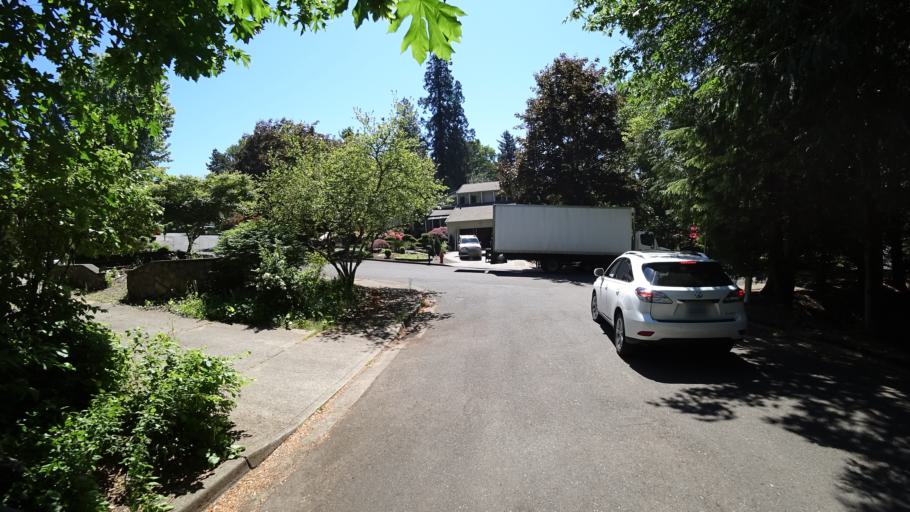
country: US
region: Oregon
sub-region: Multnomah County
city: Portland
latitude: 45.4874
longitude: -122.7115
